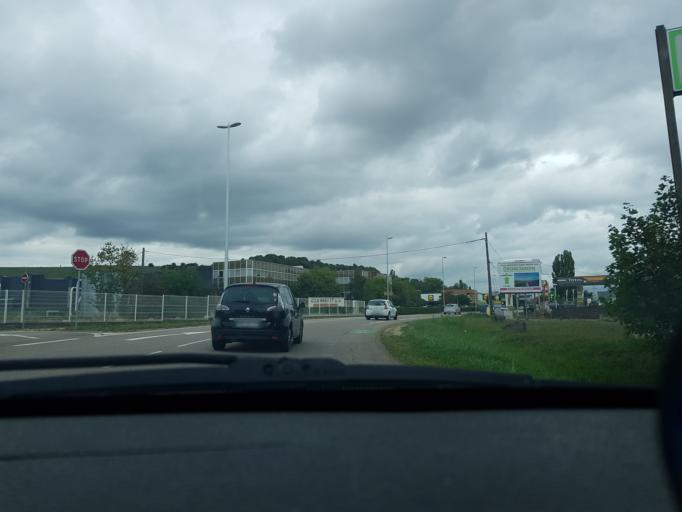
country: FR
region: Lorraine
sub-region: Departement de Meurthe-et-Moselle
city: Seichamps
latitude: 48.7125
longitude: 6.2485
